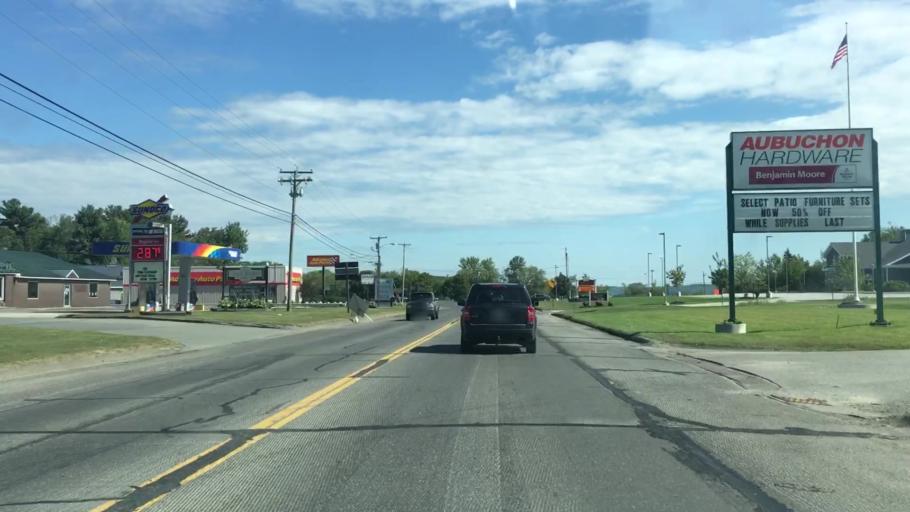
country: US
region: Maine
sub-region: Penobscot County
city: Newport
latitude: 44.8388
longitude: -69.2829
